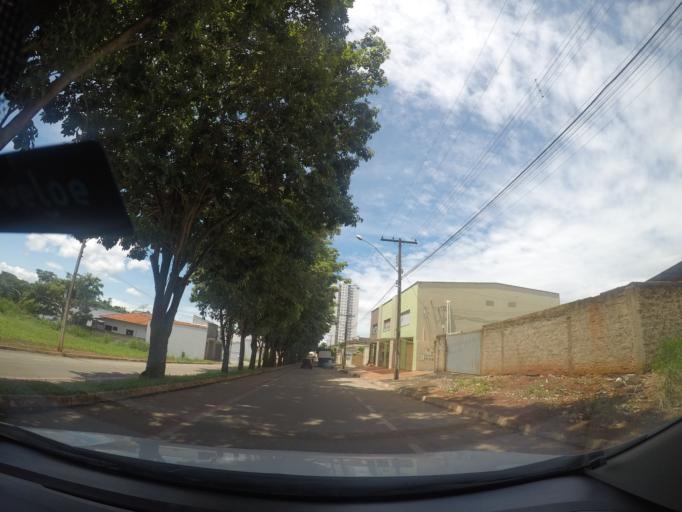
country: BR
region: Goias
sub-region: Inhumas
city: Inhumas
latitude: -16.3691
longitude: -49.5007
